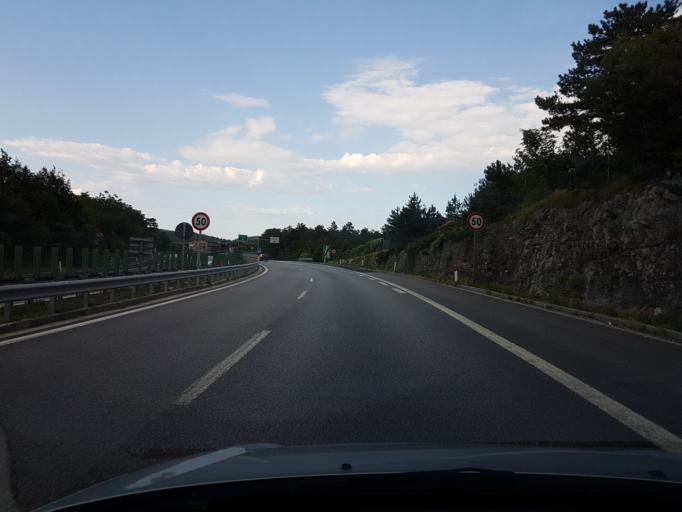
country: IT
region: Friuli Venezia Giulia
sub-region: Provincia di Trieste
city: Zolla
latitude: 45.6950
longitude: 13.8305
